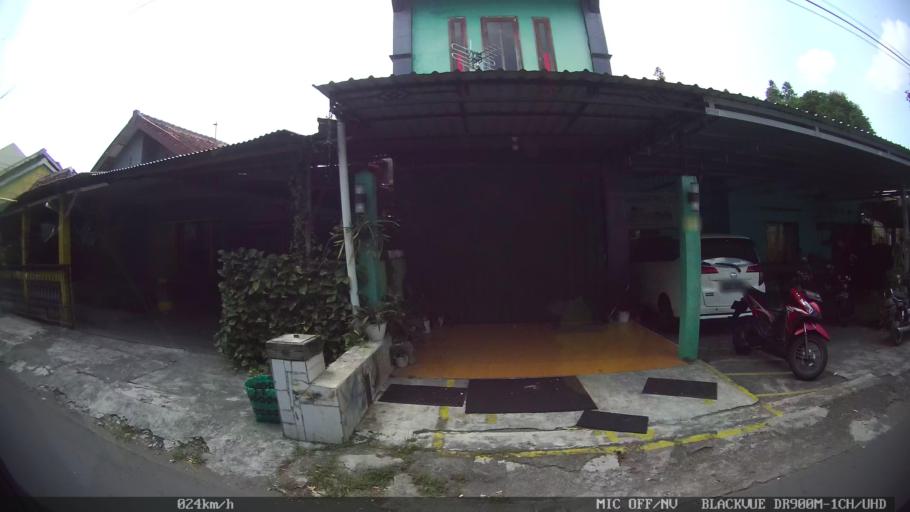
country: ID
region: Daerah Istimewa Yogyakarta
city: Yogyakarta
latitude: -7.8057
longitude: 110.3828
